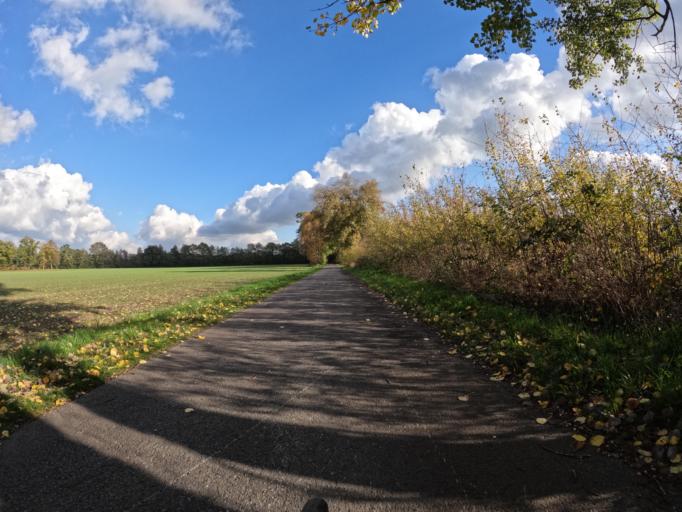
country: DE
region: North Rhine-Westphalia
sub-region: Regierungsbezirk Detmold
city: Hovelhof
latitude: 51.8222
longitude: 8.6039
